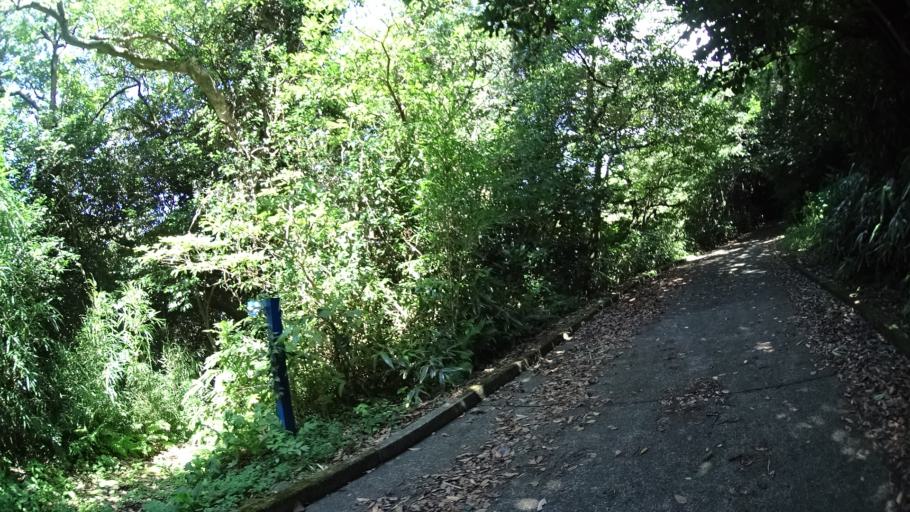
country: JP
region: Shizuoka
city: Shimoda
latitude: 34.5153
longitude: 139.2782
